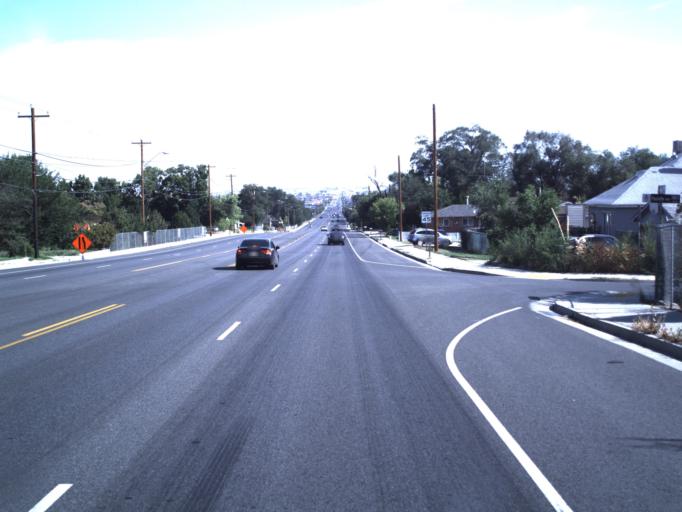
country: US
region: Utah
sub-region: Salt Lake County
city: West Valley City
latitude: 40.6875
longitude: -112.0247
